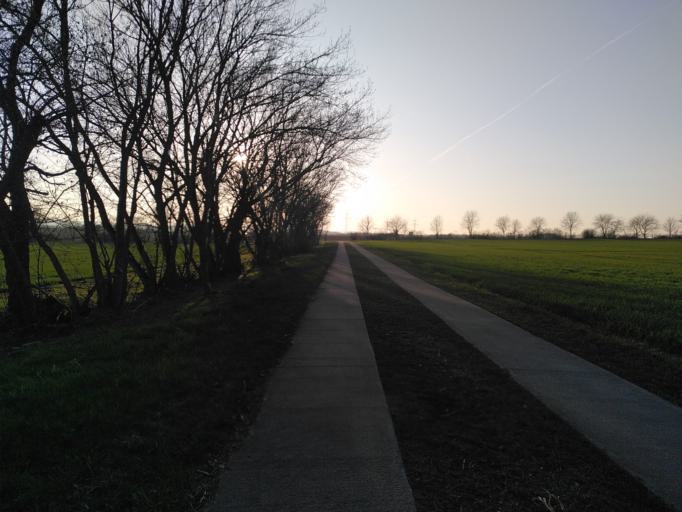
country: DE
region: Saxony-Anhalt
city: Ditfurt
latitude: 51.7964
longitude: 11.2072
